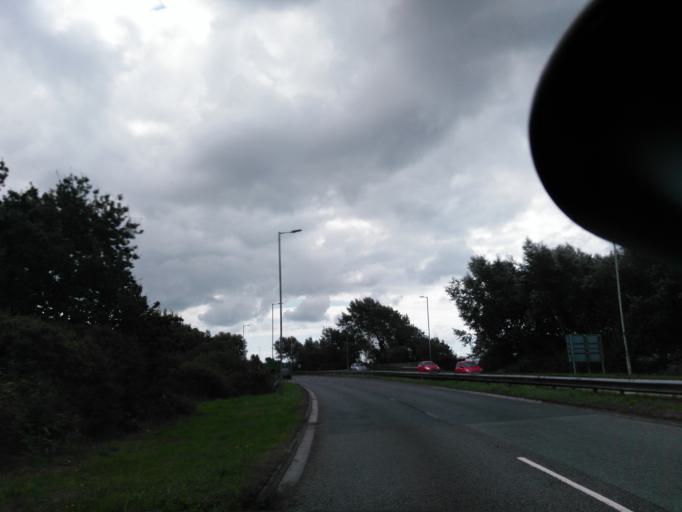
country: GB
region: England
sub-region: Poole
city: Poole
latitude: 50.7357
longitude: -1.9943
